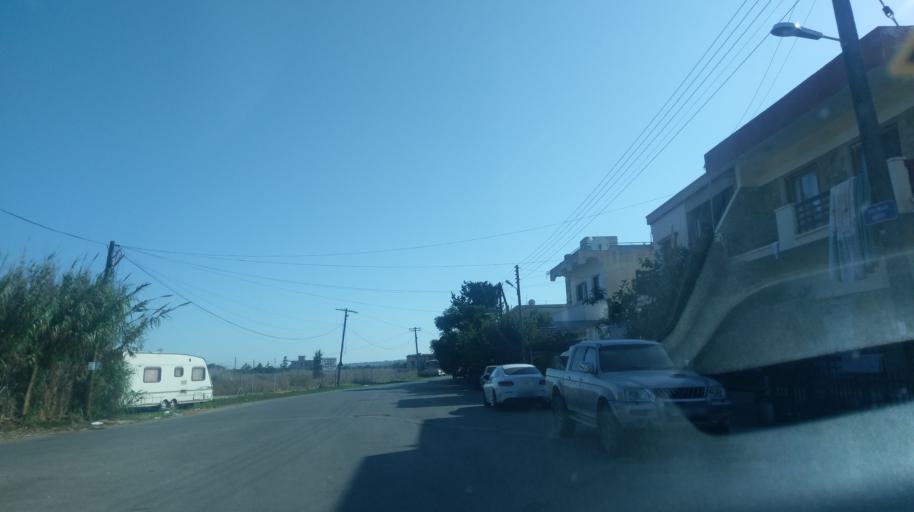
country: CY
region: Ammochostos
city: Famagusta
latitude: 35.0994
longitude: 33.9498
